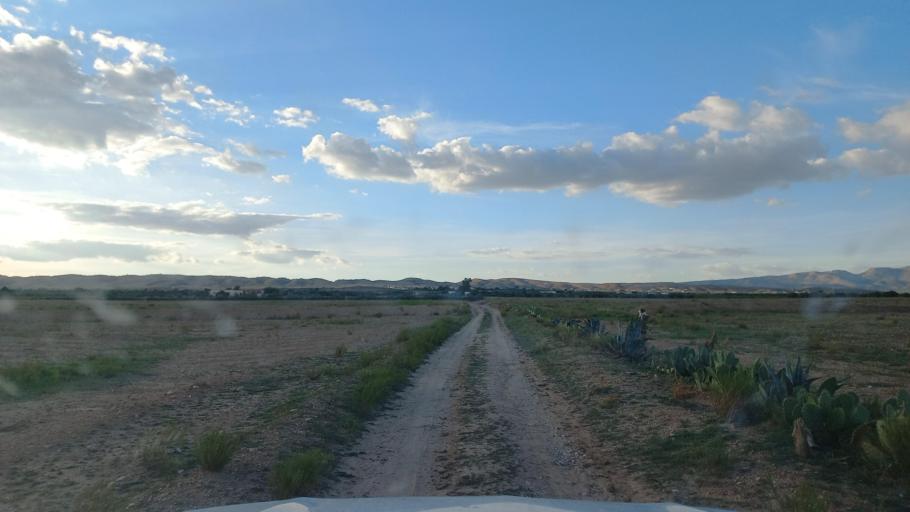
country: TN
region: Al Qasrayn
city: Sbiba
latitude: 35.3525
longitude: 9.0267
